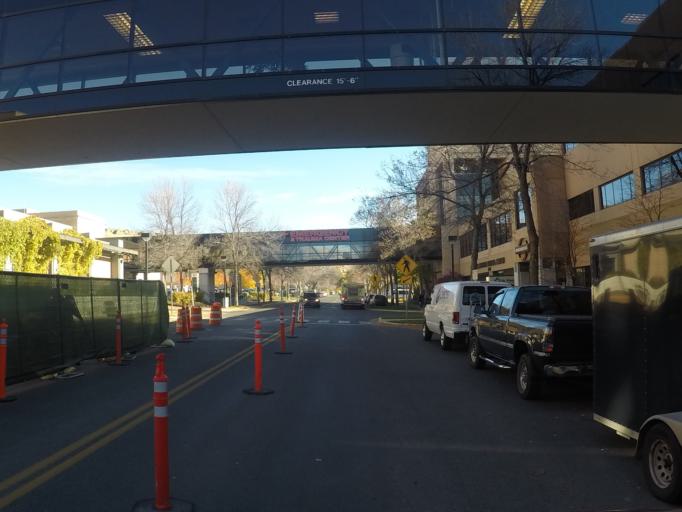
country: US
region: Montana
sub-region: Yellowstone County
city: Billings
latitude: 45.7927
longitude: -108.5188
